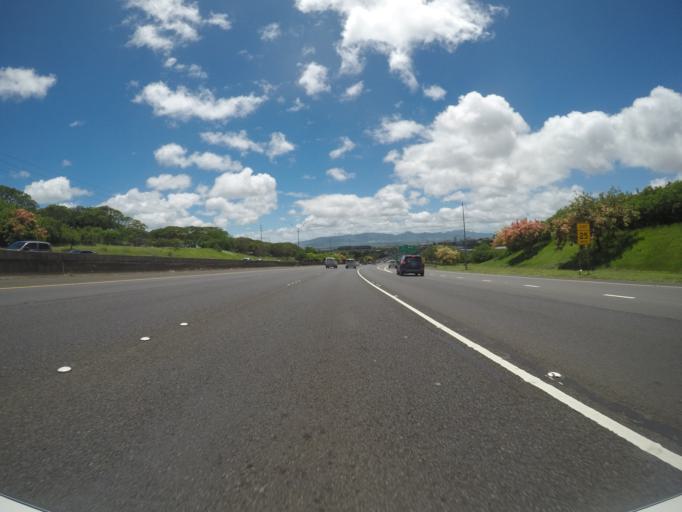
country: US
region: Hawaii
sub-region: Honolulu County
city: Halawa Heights
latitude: 21.3687
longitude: -157.9096
